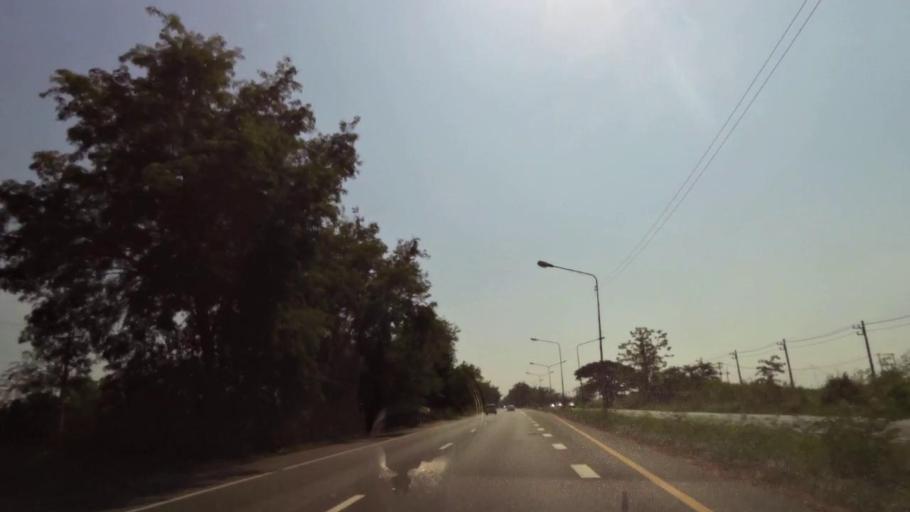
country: TH
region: Nakhon Sawan
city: Kao Liao
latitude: 15.9310
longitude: 100.1125
